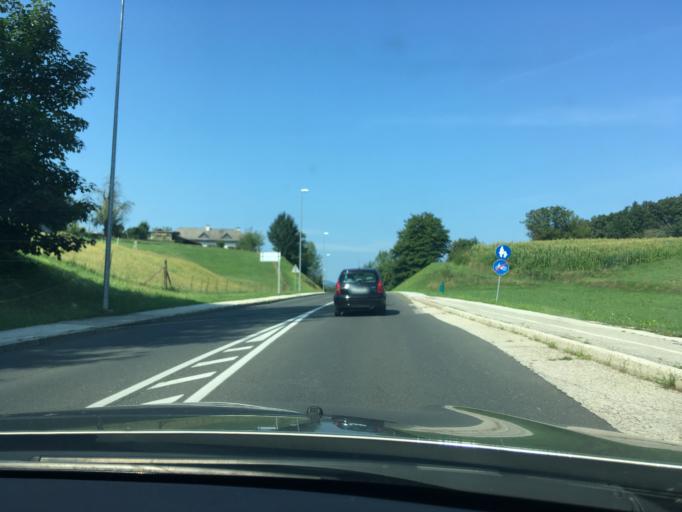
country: SI
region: Novo Mesto
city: Novo Mesto
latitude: 45.8022
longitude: 15.1582
